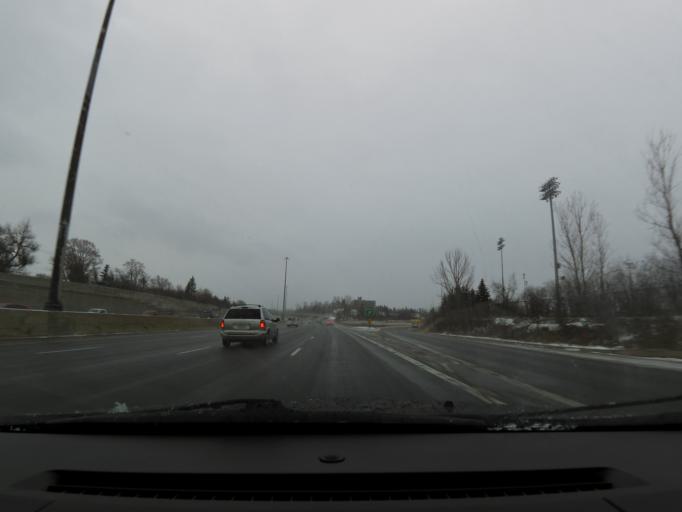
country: CA
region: Ontario
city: Kitchener
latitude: 43.4492
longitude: -80.4637
